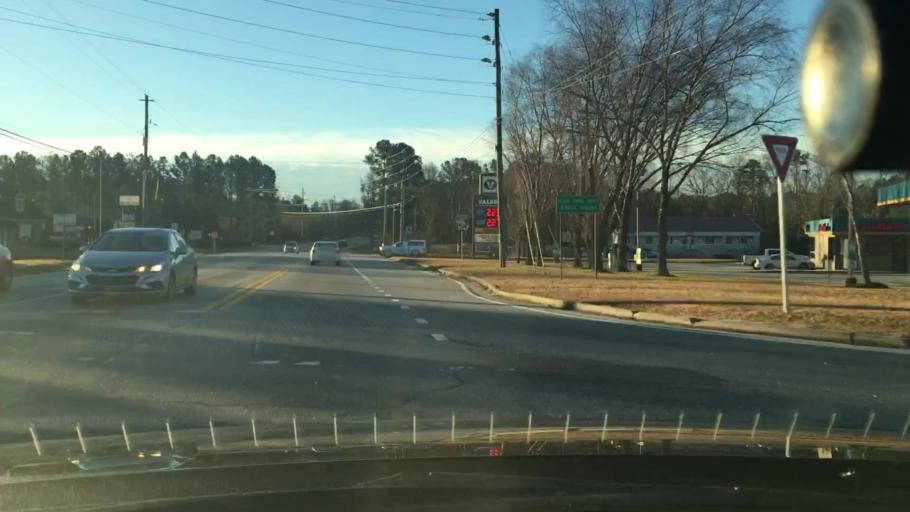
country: US
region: Georgia
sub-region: Fayette County
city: Peachtree City
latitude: 33.4081
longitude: -84.6826
